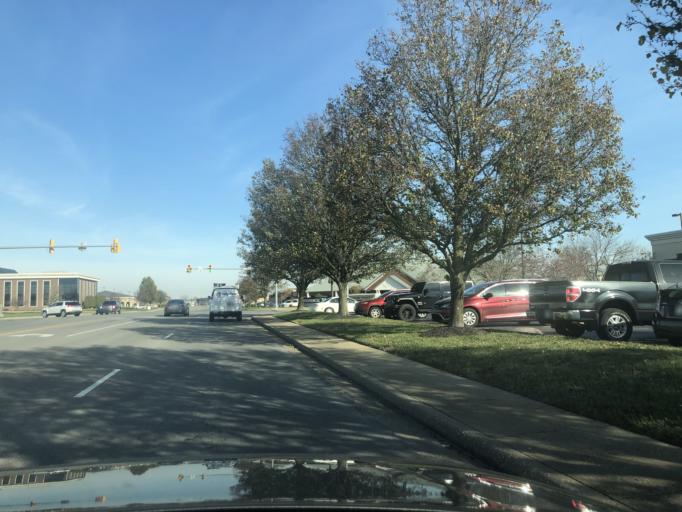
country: US
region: Indiana
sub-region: Warrick County
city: Newburgh
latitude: 37.9806
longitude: -87.4625
